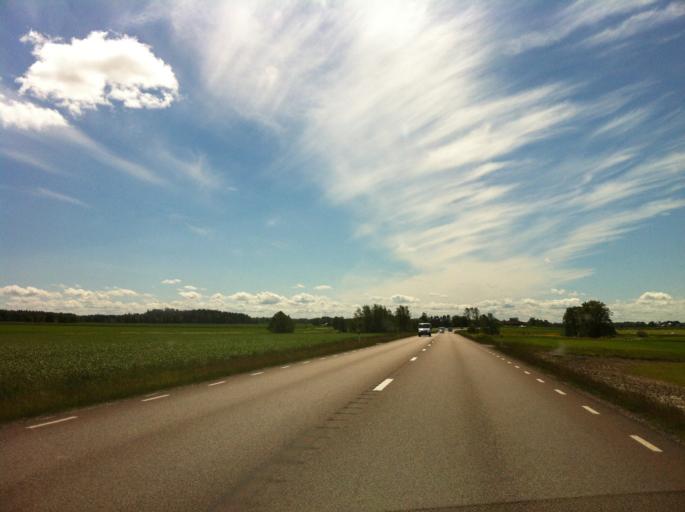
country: SE
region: Vaestra Goetaland
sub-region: Vanersborgs Kommun
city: Bralanda
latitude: 58.5316
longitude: 12.3183
